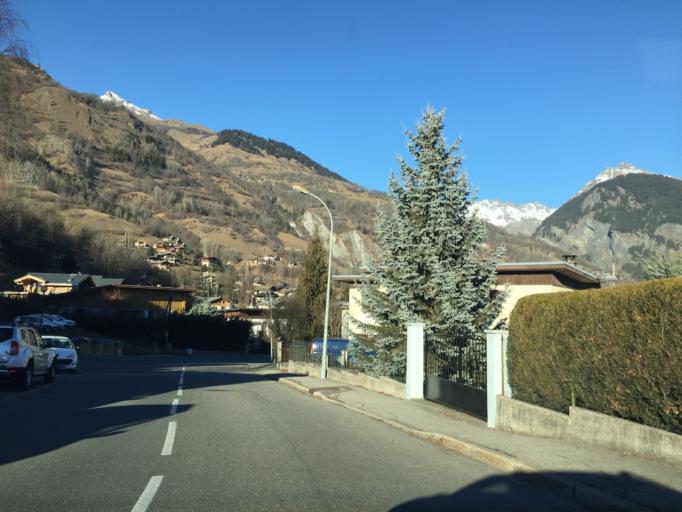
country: FR
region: Rhone-Alpes
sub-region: Departement de la Savoie
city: Bourg-Saint-Maurice
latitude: 45.6146
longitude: 6.7623
